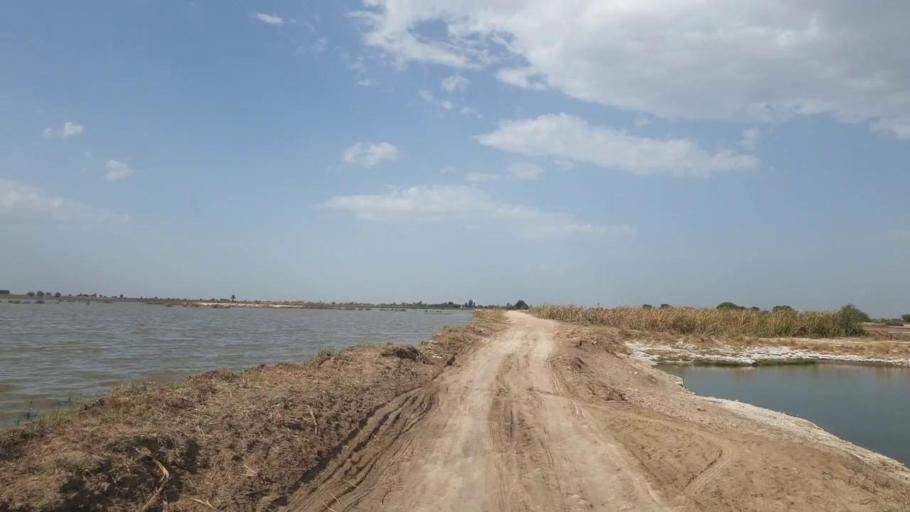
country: PK
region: Sindh
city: Shahdadpur
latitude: 25.9946
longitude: 68.4639
